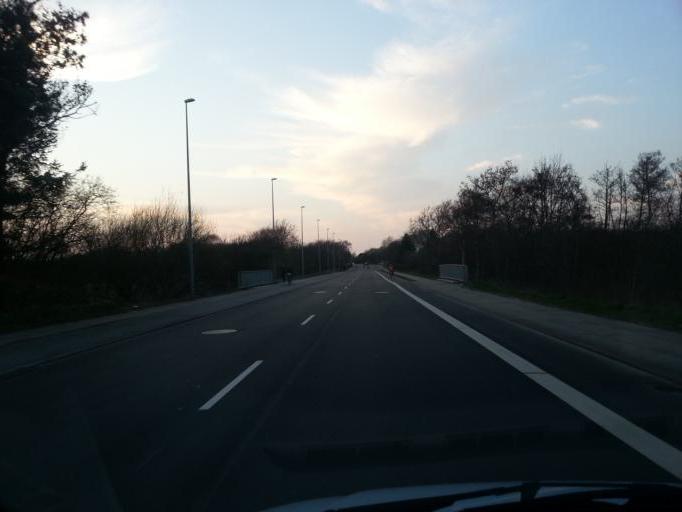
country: DK
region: South Denmark
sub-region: Esbjerg Kommune
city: Esbjerg
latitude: 55.4910
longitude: 8.4322
